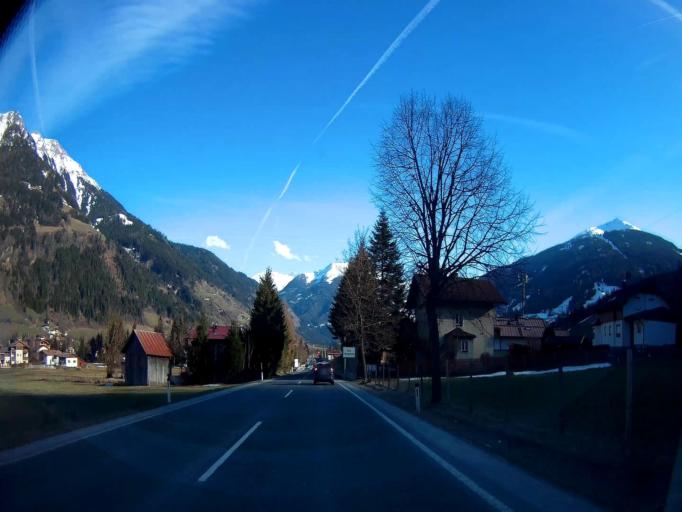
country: AT
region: Salzburg
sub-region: Politischer Bezirk Sankt Johann im Pongau
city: Bad Hofgastein
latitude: 47.1607
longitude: 13.1030
